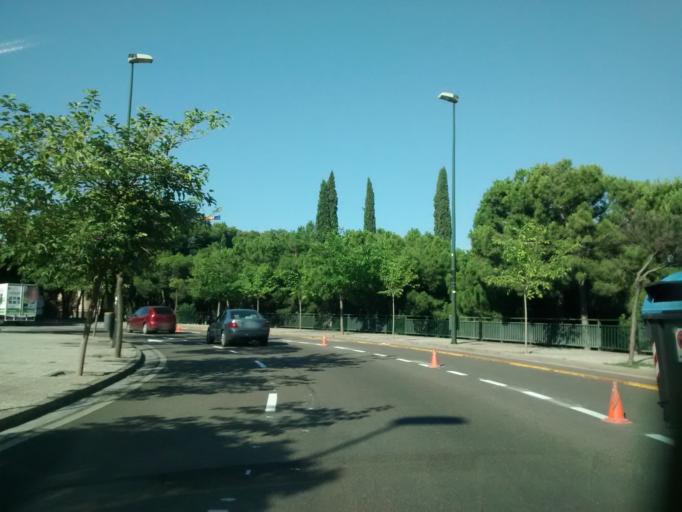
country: ES
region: Aragon
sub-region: Provincia de Zaragoza
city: Almozara
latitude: 41.6581
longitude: -0.8951
